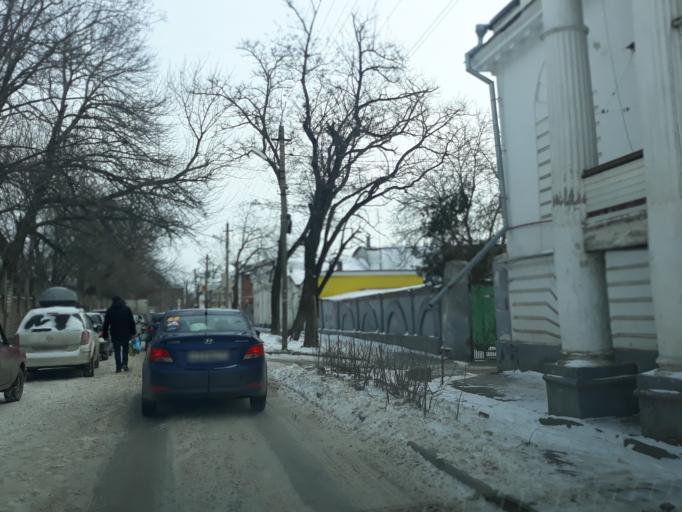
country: RU
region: Rostov
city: Taganrog
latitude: 47.2106
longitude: 38.9183
